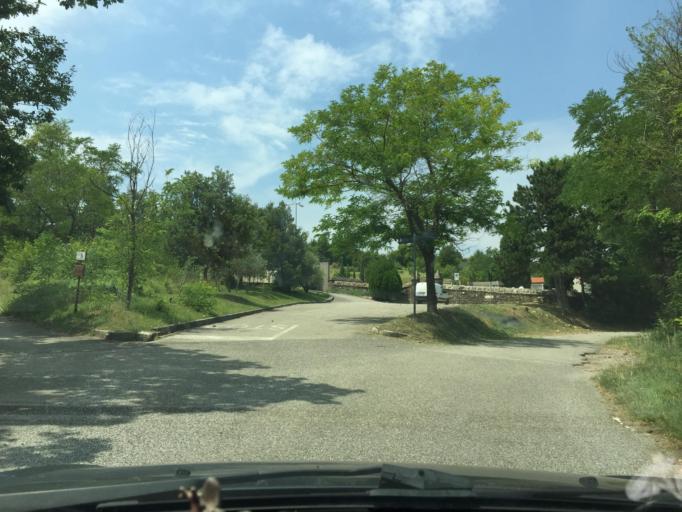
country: IT
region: Friuli Venezia Giulia
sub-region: Provincia di Trieste
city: Domio
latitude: 45.5931
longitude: 13.8313
